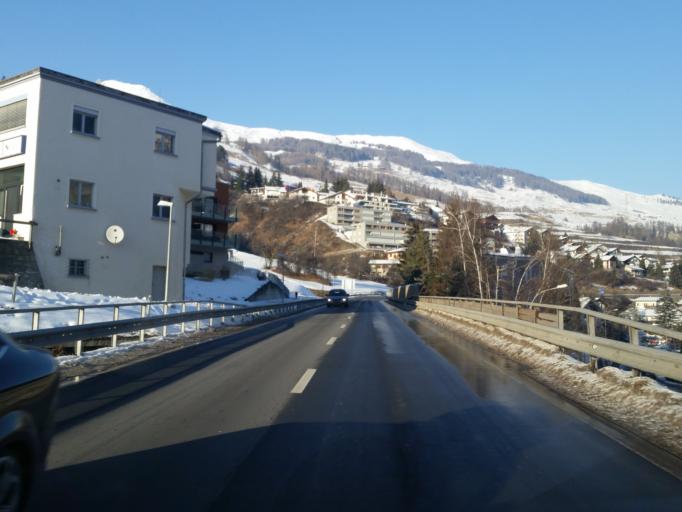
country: CH
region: Grisons
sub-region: Inn District
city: Scuol
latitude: 46.7944
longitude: 10.2903
